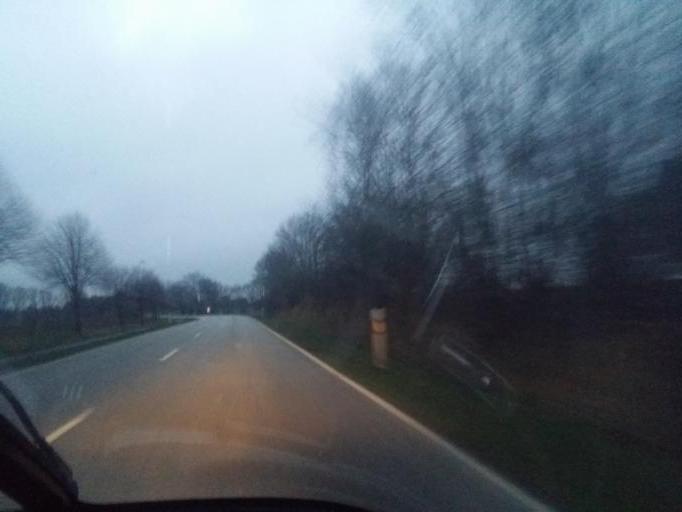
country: DE
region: Schleswig-Holstein
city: Warringholz
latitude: 54.0915
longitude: 9.4668
